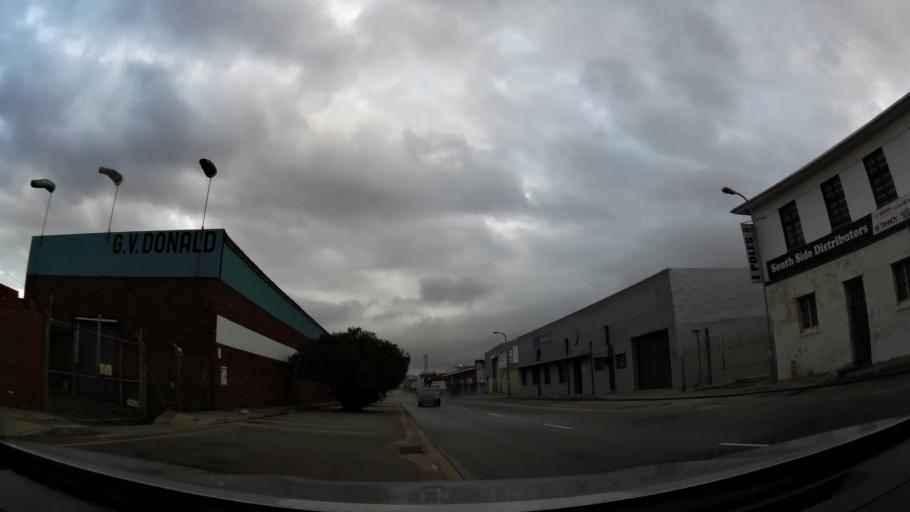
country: ZA
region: Eastern Cape
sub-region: Nelson Mandela Bay Metropolitan Municipality
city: Port Elizabeth
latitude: -33.9333
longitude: 25.6091
